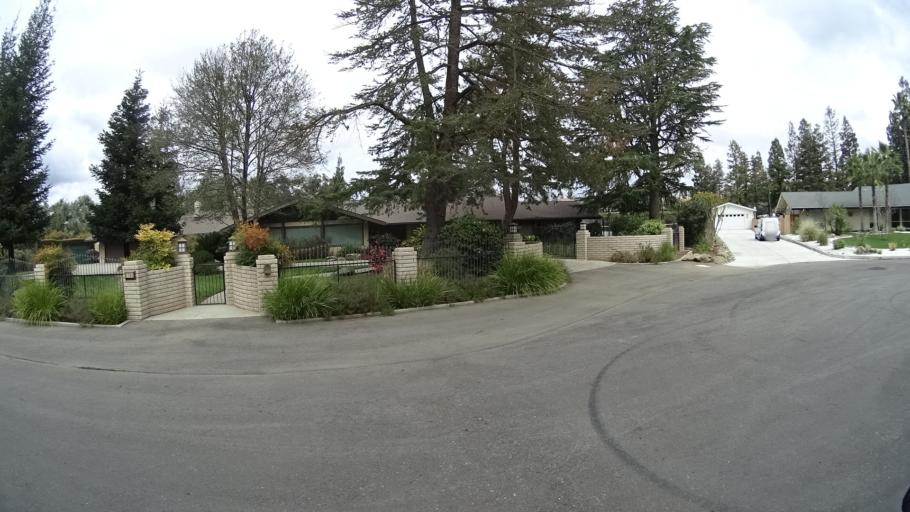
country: US
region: California
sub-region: Fresno County
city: Fresno
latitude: 36.8462
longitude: -119.8320
